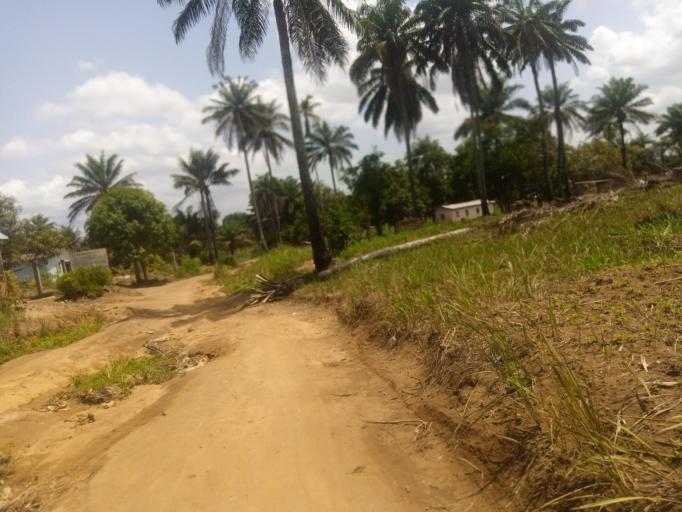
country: SL
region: Western Area
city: Waterloo
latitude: 8.3190
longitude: -13.0076
